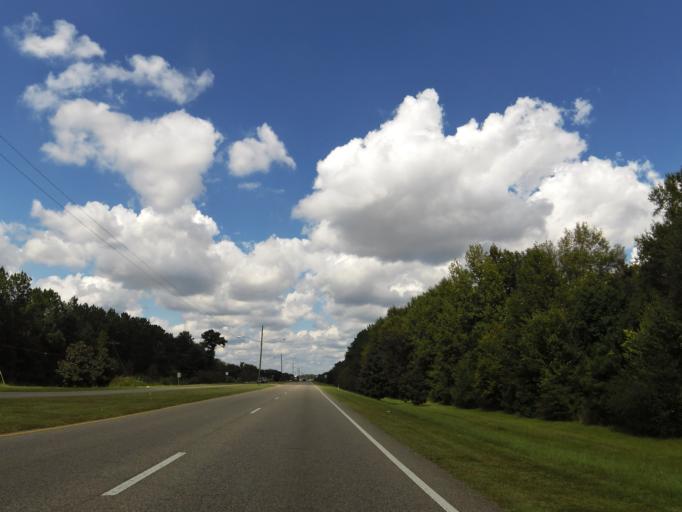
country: US
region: Alabama
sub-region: Dallas County
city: Selmont-West Selmont
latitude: 32.3851
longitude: -87.0115
